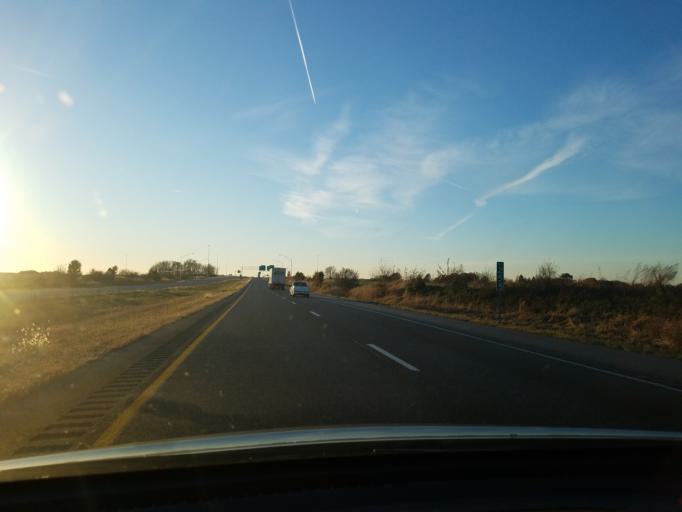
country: US
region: Indiana
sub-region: Gibson County
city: Haubstadt
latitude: 38.1672
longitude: -87.5405
